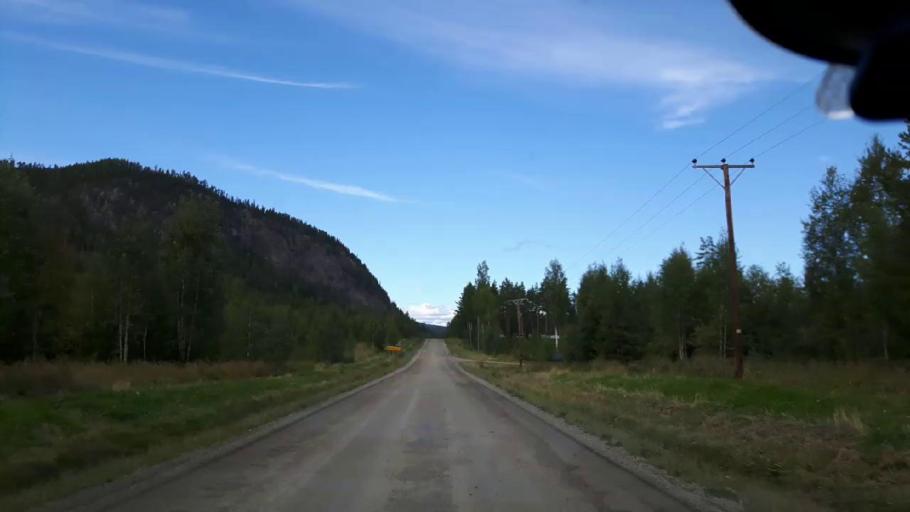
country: SE
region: Jaemtland
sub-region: Ragunda Kommun
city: Hammarstrand
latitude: 63.1269
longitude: 16.3261
